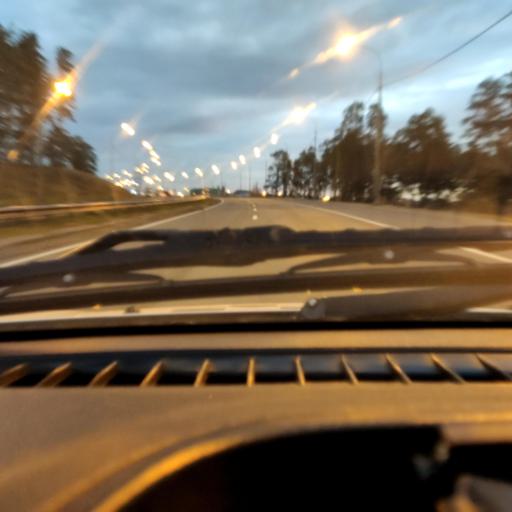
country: RU
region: Samara
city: Zhigulevsk
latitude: 53.5377
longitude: 49.5168
